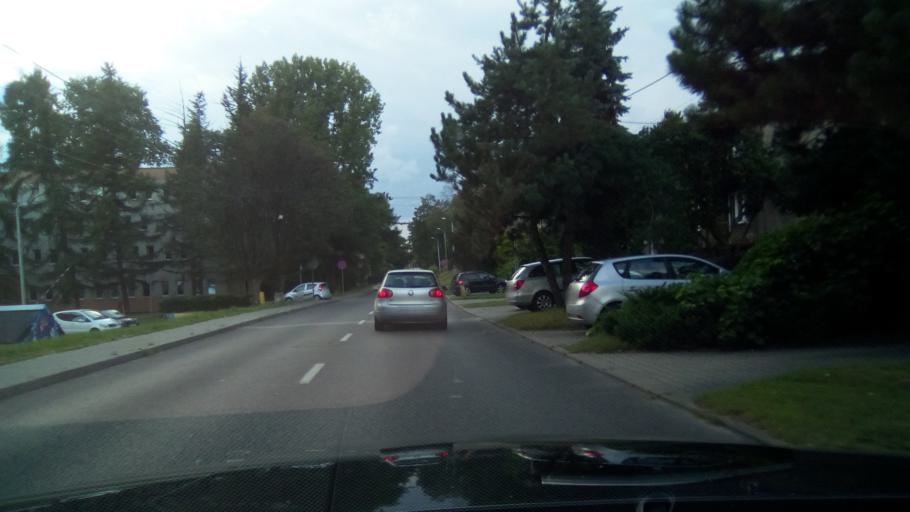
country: PL
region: Silesian Voivodeship
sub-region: Myslowice
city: Myslowice
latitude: 50.2068
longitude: 19.1553
